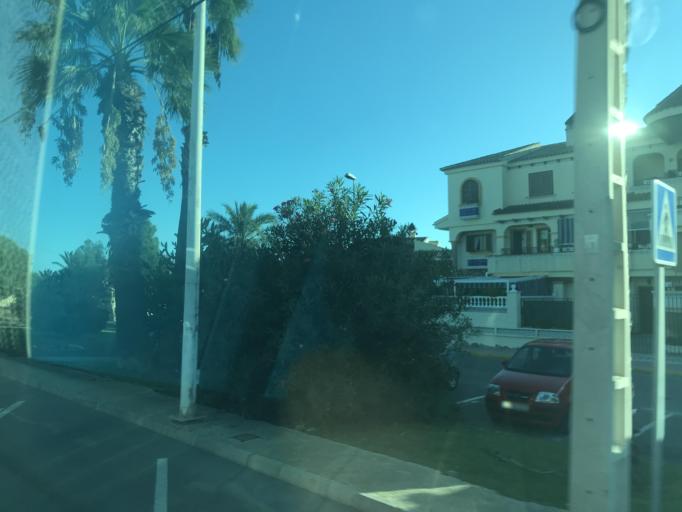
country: ES
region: Valencia
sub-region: Provincia de Alicante
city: Torrevieja
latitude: 38.0031
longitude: -0.6542
